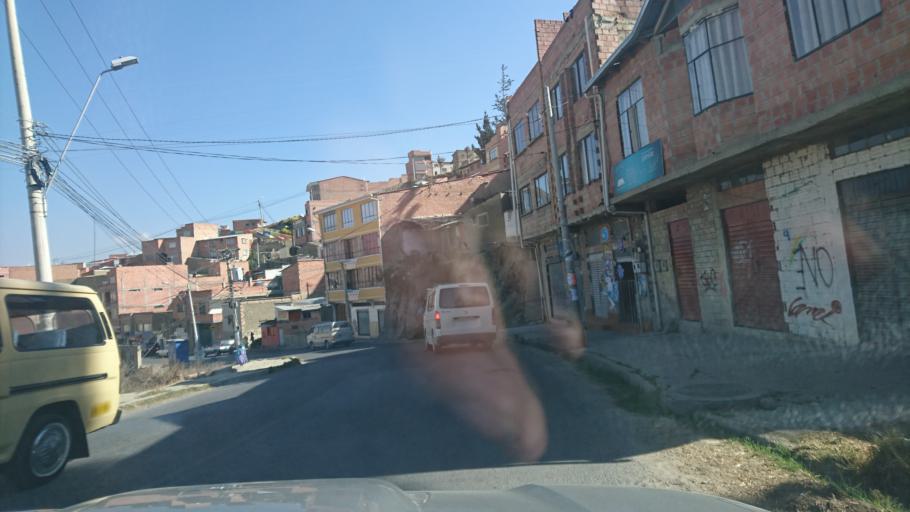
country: BO
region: La Paz
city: La Paz
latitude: -16.5104
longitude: -68.1061
